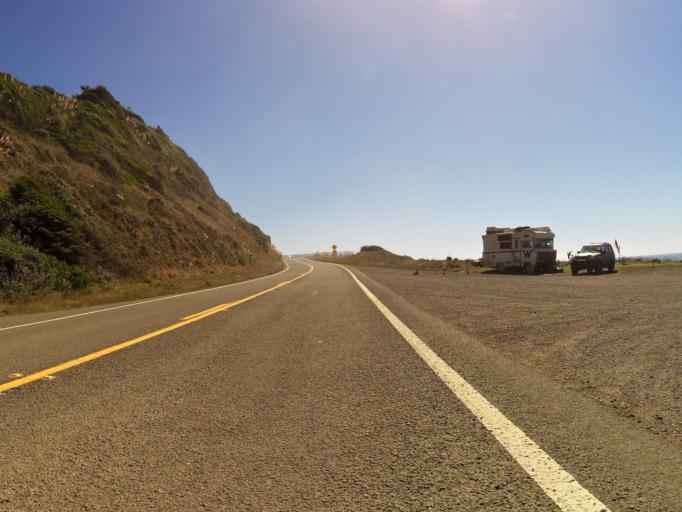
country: US
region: California
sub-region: Mendocino County
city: Fort Bragg
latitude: 39.7023
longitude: -123.8036
